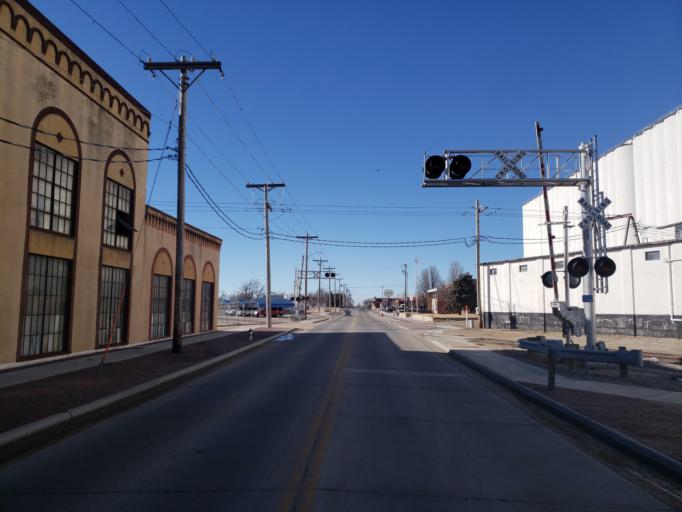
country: US
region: Kansas
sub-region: Ford County
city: Dodge City
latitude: 37.7519
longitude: -100.0245
